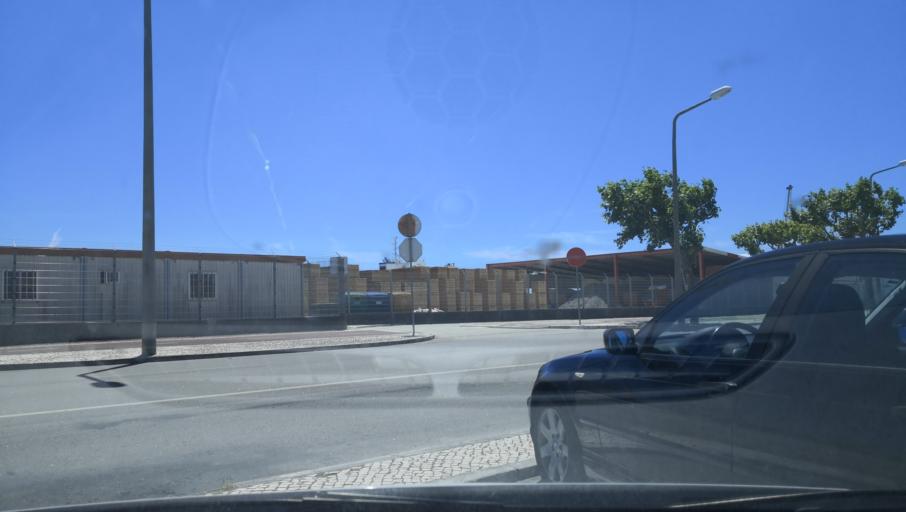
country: PT
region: Coimbra
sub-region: Figueira da Foz
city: Figueira da Foz
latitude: 40.1481
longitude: -8.8483
